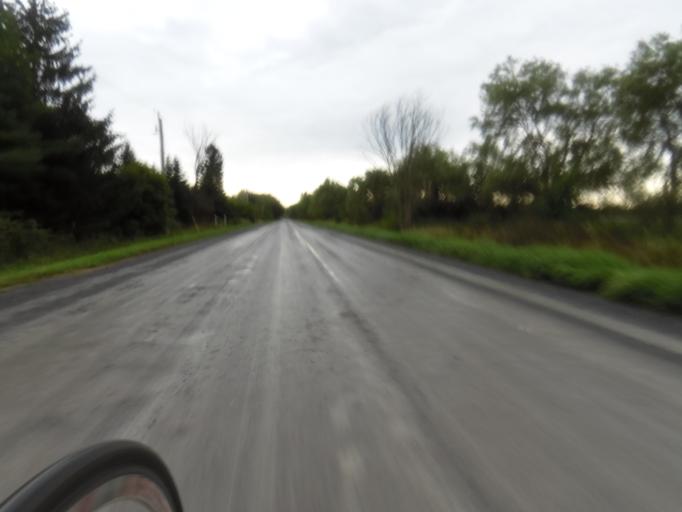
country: CA
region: Ontario
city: Bells Corners
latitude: 45.1721
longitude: -75.6990
